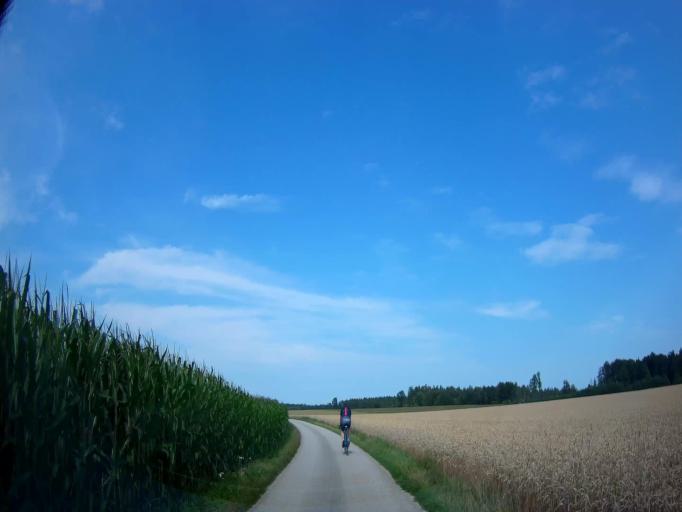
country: AT
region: Upper Austria
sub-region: Politischer Bezirk Kirchdorf an der Krems
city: Kremsmunster
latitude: 48.0833
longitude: 14.1068
